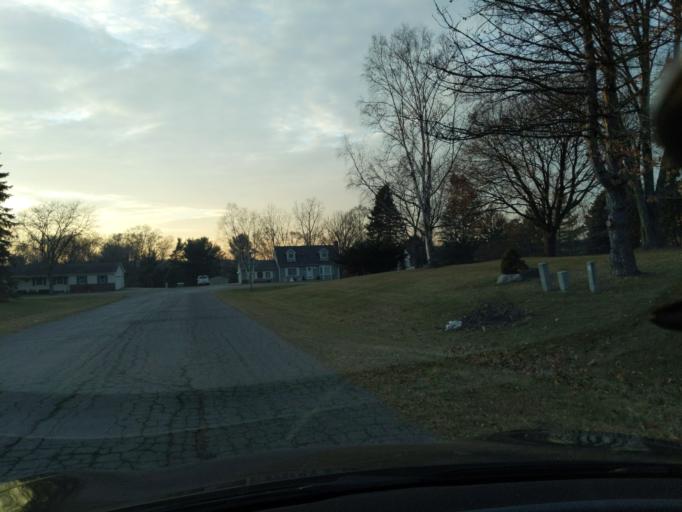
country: US
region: Michigan
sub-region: Livingston County
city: Brighton
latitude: 42.6470
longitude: -83.7228
